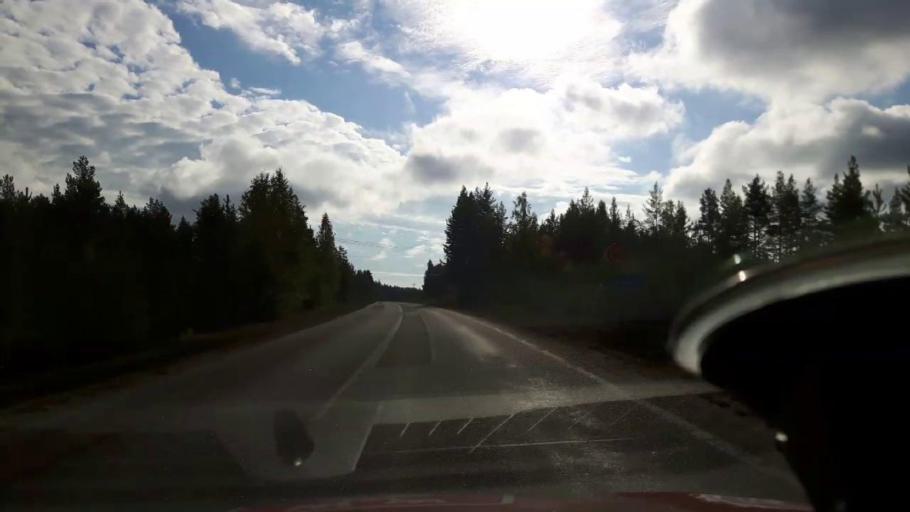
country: SE
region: Jaemtland
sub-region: Harjedalens Kommun
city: Sveg
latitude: 62.1166
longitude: 15.0448
